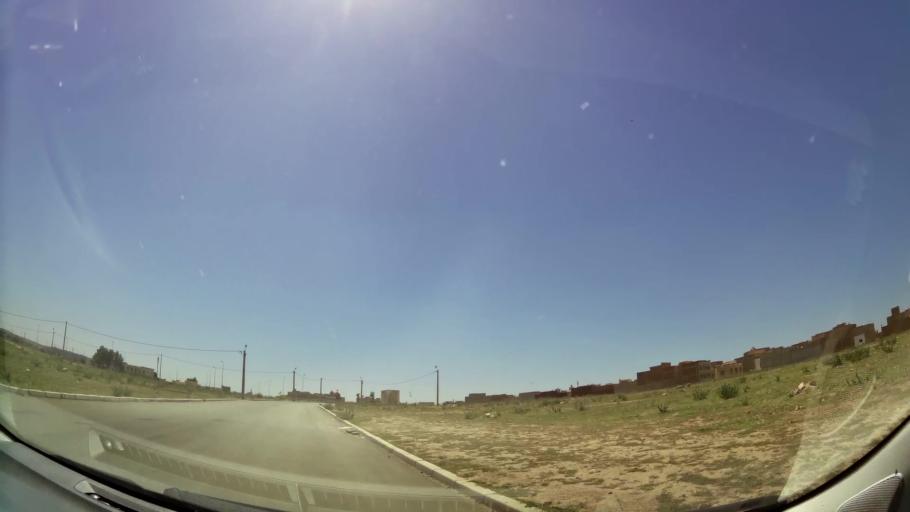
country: MA
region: Oriental
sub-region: Oujda-Angad
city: Oujda
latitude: 34.6691
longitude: -1.8651
